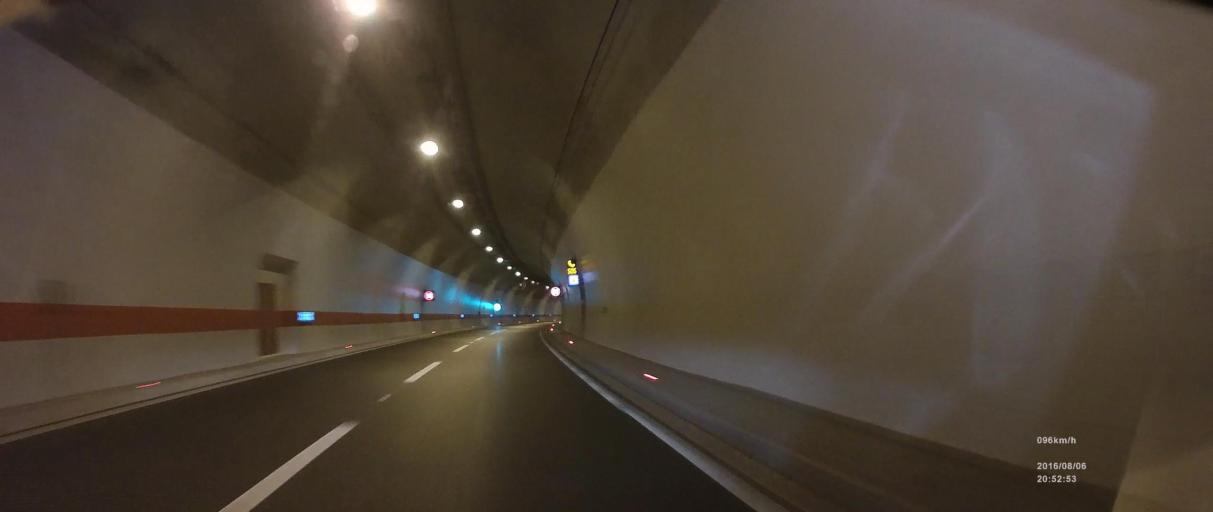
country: BA
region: Federation of Bosnia and Herzegovina
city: Ljubuski
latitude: 43.1379
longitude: 17.4833
